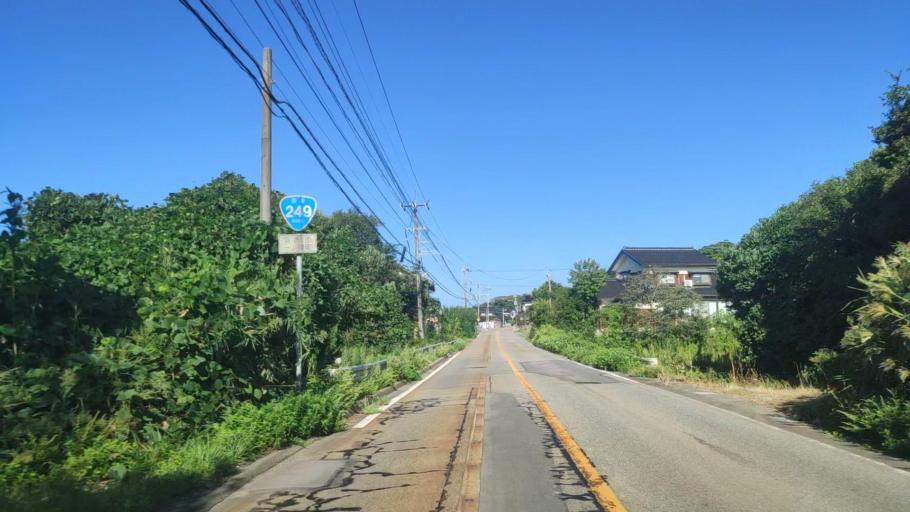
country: JP
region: Ishikawa
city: Hakui
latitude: 36.9252
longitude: 136.7623
